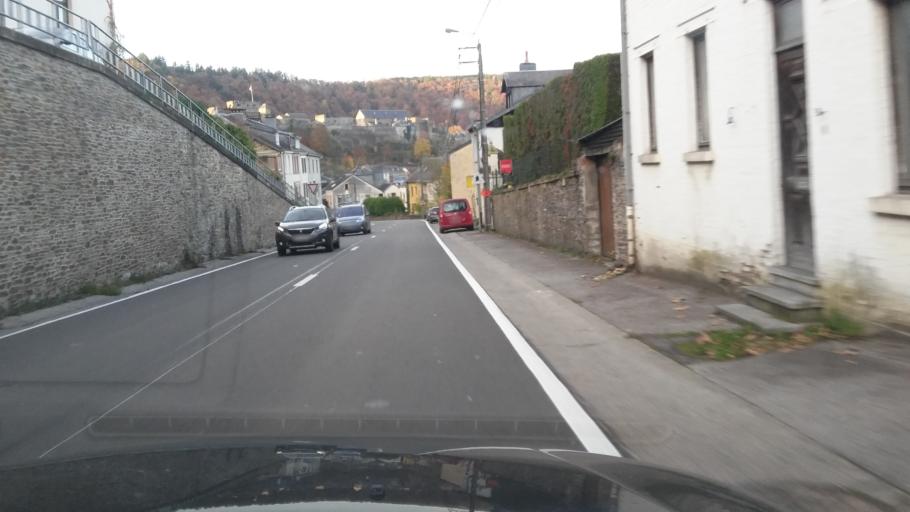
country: BE
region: Wallonia
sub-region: Province du Luxembourg
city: Bouillon
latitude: 49.7869
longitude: 5.0652
